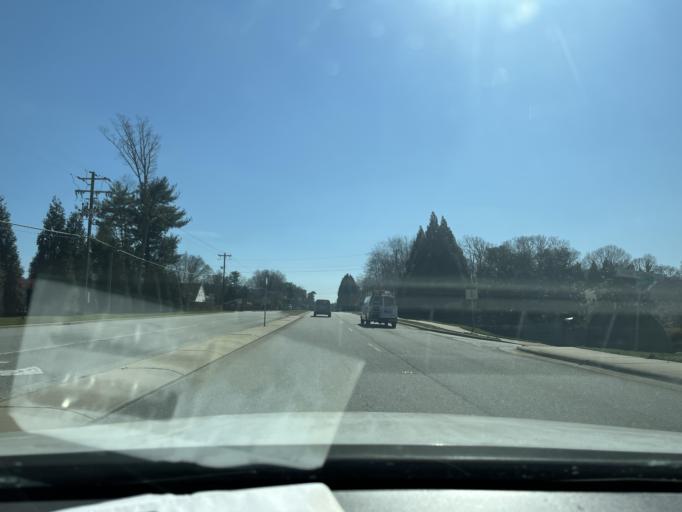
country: US
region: North Carolina
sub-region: Guilford County
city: Jamestown
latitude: 36.0316
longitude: -79.9223
